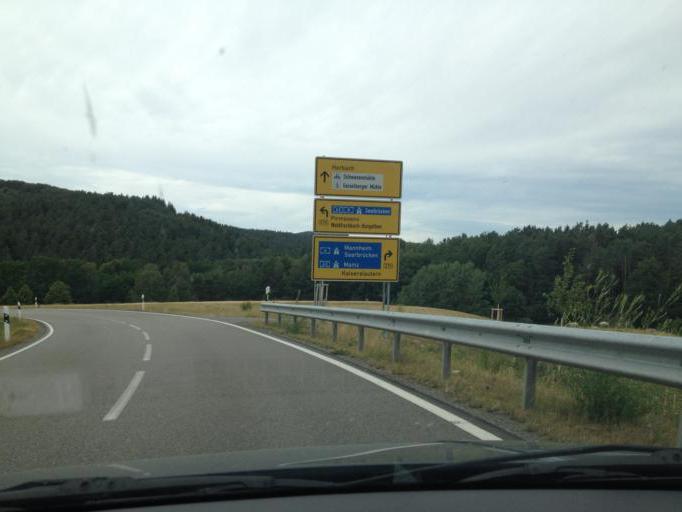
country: DE
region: Rheinland-Pfalz
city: Steinalben
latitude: 49.3246
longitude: 7.6726
